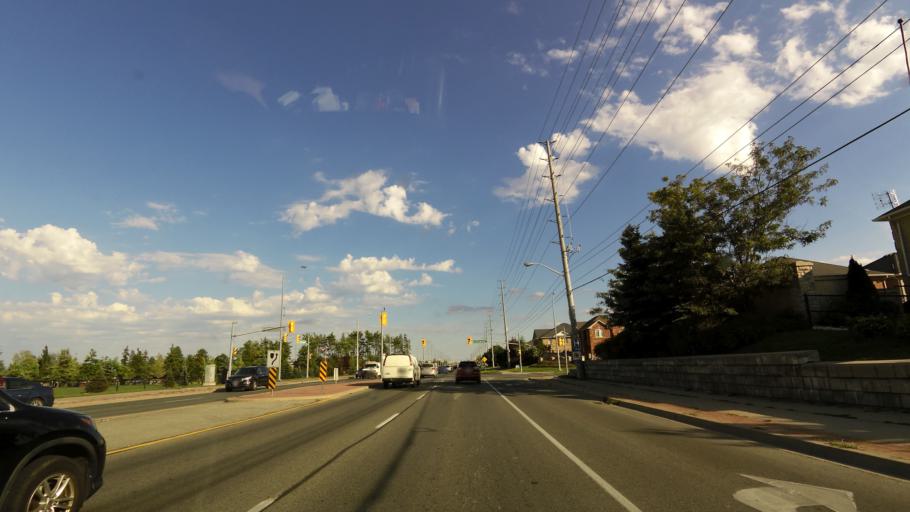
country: CA
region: Ontario
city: Brampton
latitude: 43.6885
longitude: -79.8117
